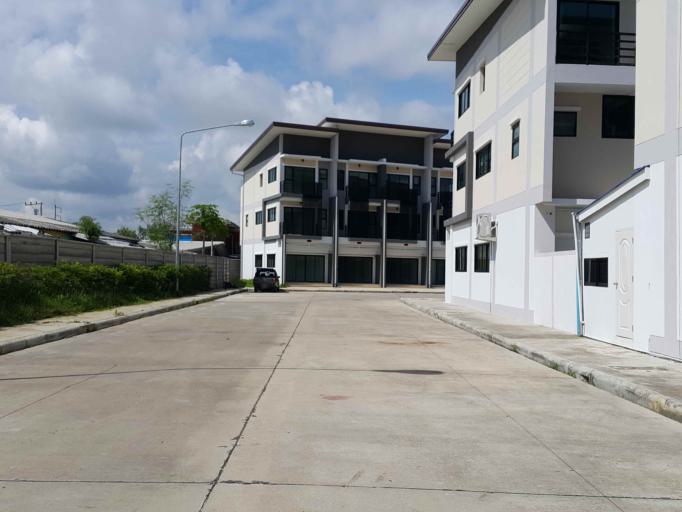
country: TH
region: Chiang Mai
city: San Sai
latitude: 18.8056
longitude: 99.0625
